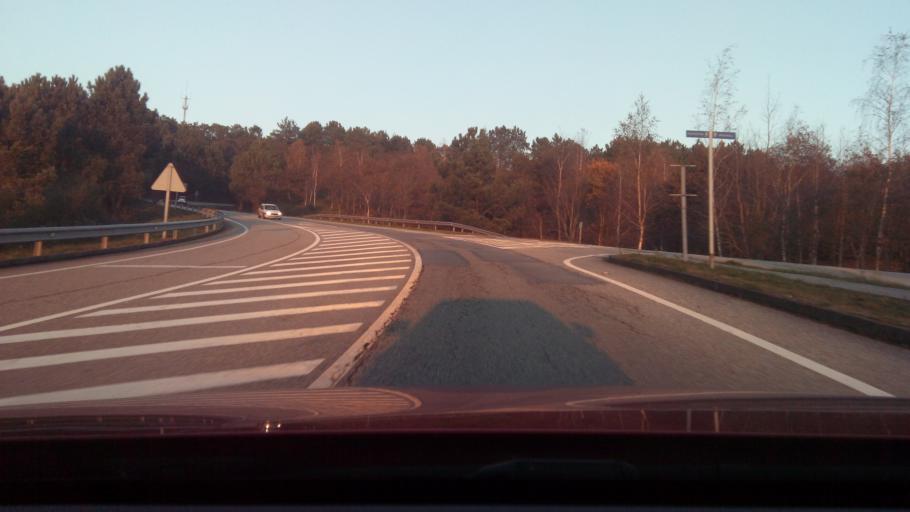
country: ES
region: Galicia
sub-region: Provincia de Pontevedra
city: Vigo
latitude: 42.1720
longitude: -8.6888
